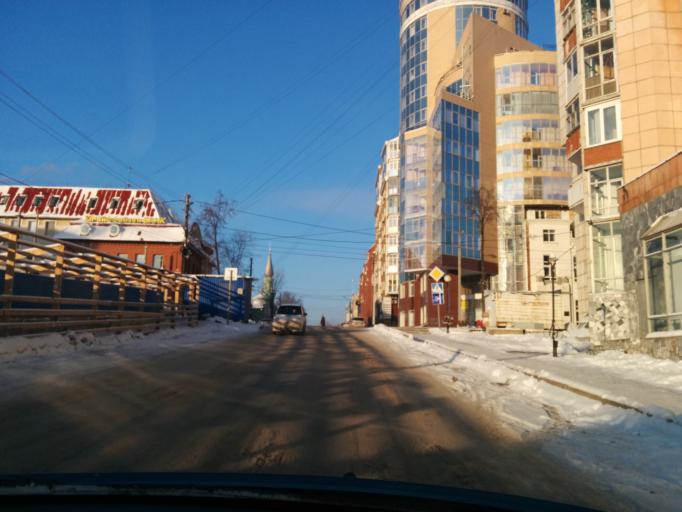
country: RU
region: Perm
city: Perm
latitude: 58.0124
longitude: 56.2291
